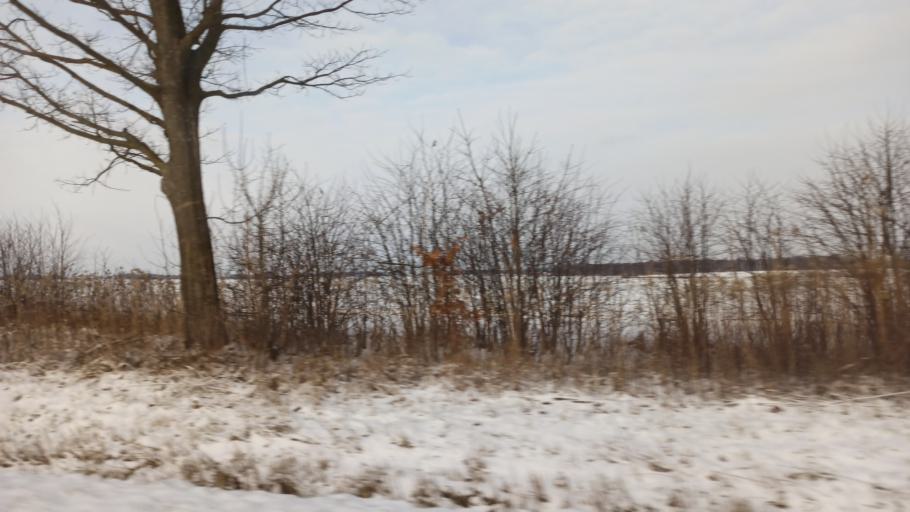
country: PL
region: Subcarpathian Voivodeship
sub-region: Powiat przeworski
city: Adamowka
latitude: 50.2418
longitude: 22.6724
